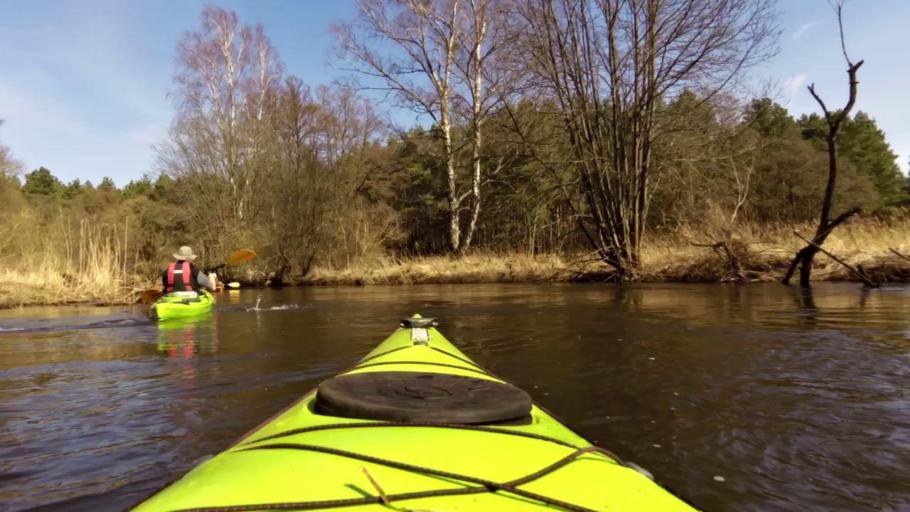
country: PL
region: West Pomeranian Voivodeship
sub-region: Powiat lobeski
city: Lobez
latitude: 53.6518
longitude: 15.5673
